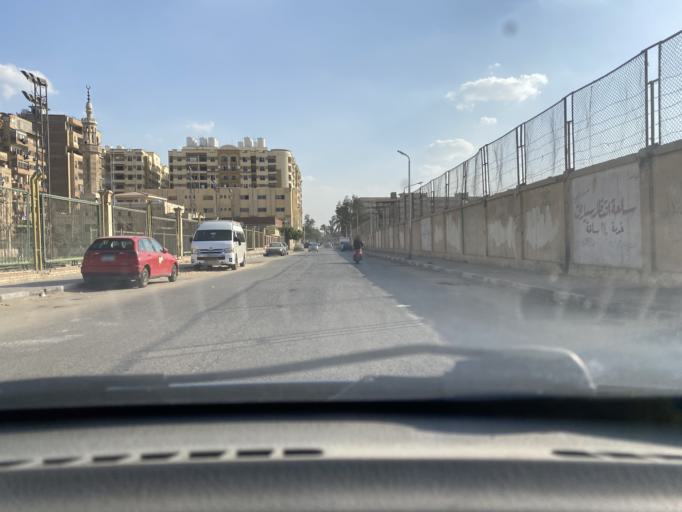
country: EG
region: Muhafazat al Qahirah
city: Cairo
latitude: 30.1052
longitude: 31.3048
